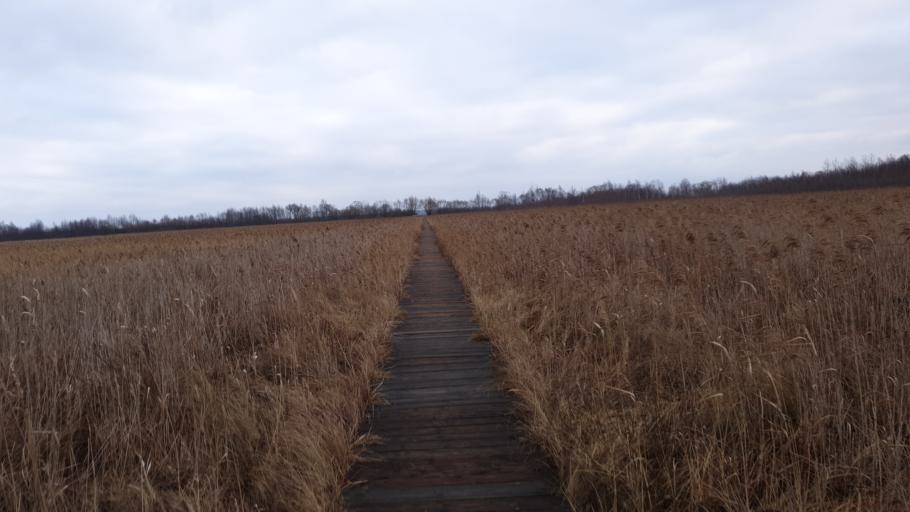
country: PL
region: Podlasie
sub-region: Powiat bialostocki
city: Tykocin
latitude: 53.2865
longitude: 22.6057
